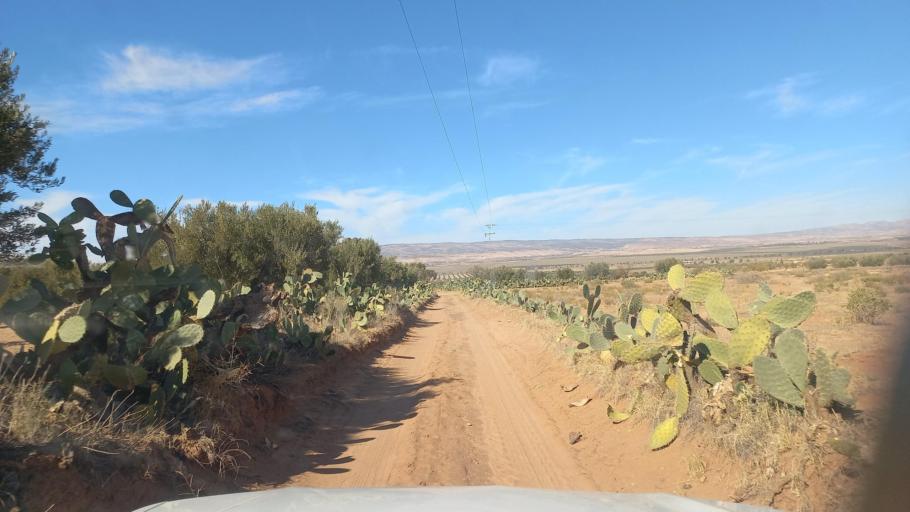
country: TN
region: Al Qasrayn
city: Kasserine
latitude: 35.2045
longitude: 8.9702
